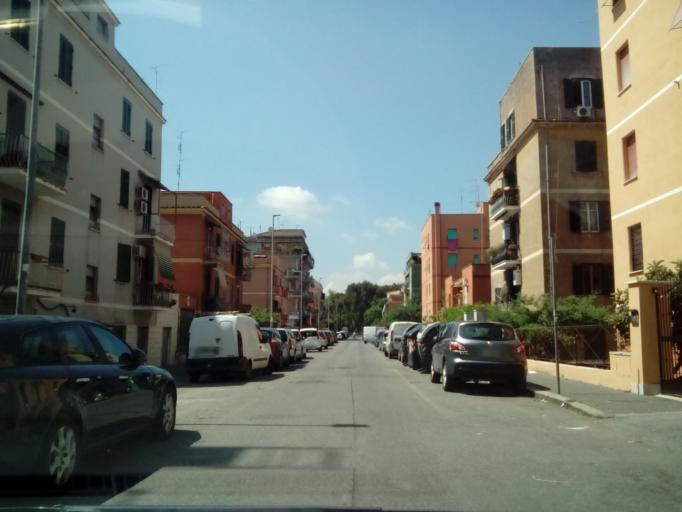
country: IT
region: Latium
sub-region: Citta metropolitana di Roma Capitale
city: Rome
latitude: 41.8762
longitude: 12.5703
